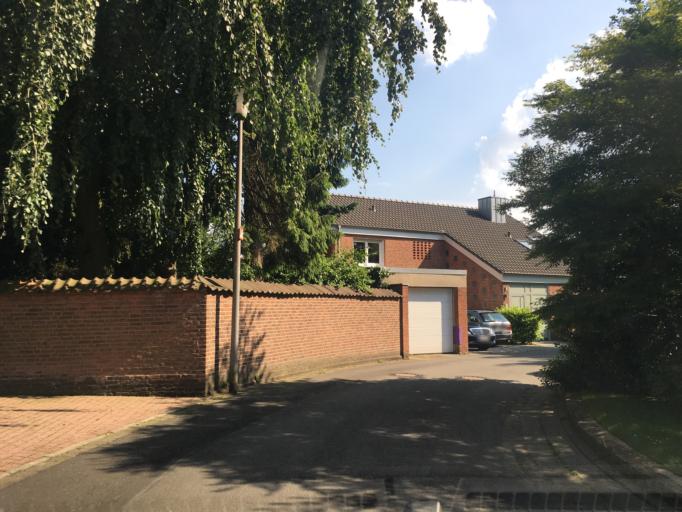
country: DE
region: North Rhine-Westphalia
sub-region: Regierungsbezirk Munster
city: Muenster
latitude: 51.9590
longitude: 7.5960
